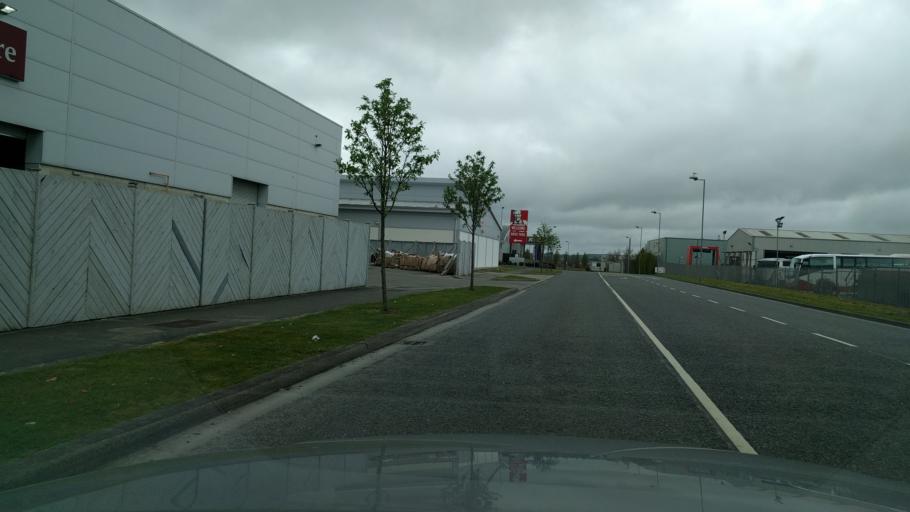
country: IE
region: Leinster
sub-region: Lu
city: Drogheda
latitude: 53.7019
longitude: -6.3767
